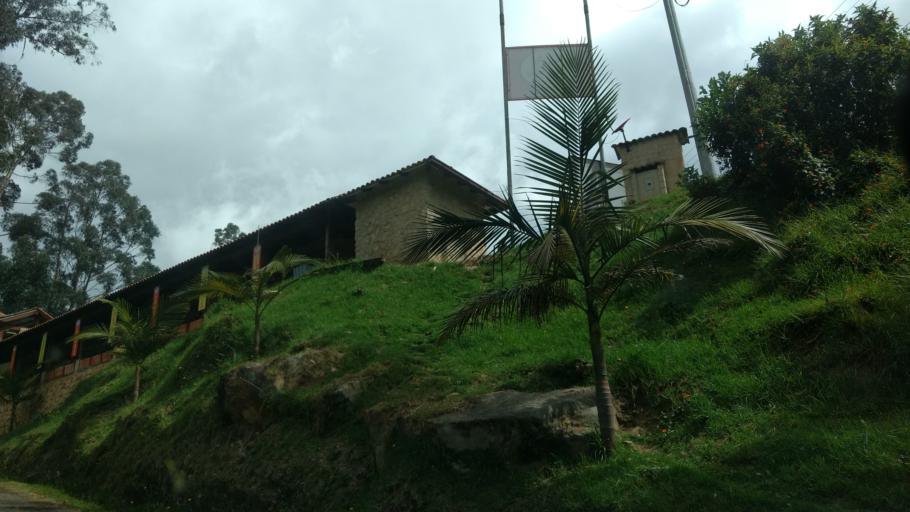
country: CO
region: Cundinamarca
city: El Rosal
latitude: 4.9000
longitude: -74.3107
